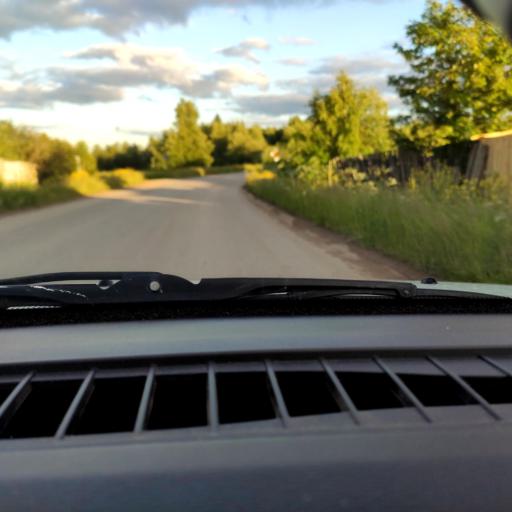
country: RU
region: Perm
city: Polazna
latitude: 58.2048
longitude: 56.4989
